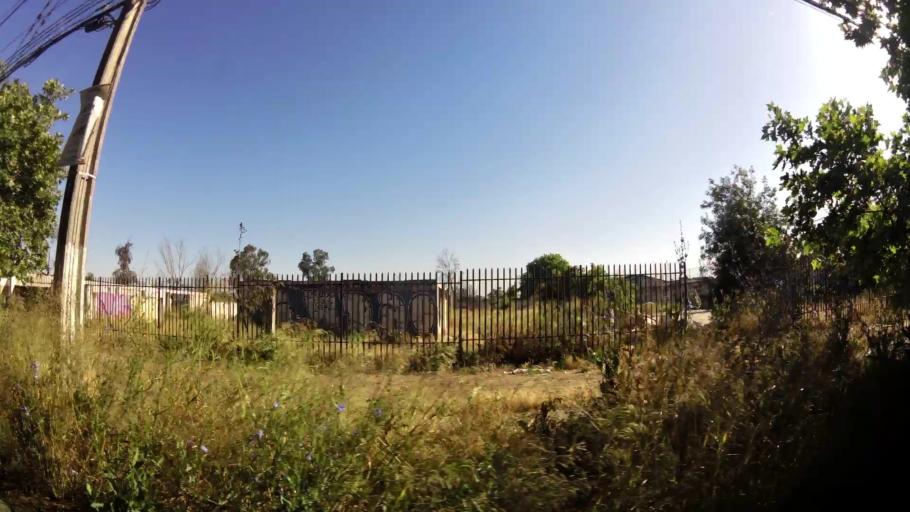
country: CL
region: Santiago Metropolitan
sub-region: Provincia de Santiago
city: La Pintana
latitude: -33.5439
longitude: -70.6727
